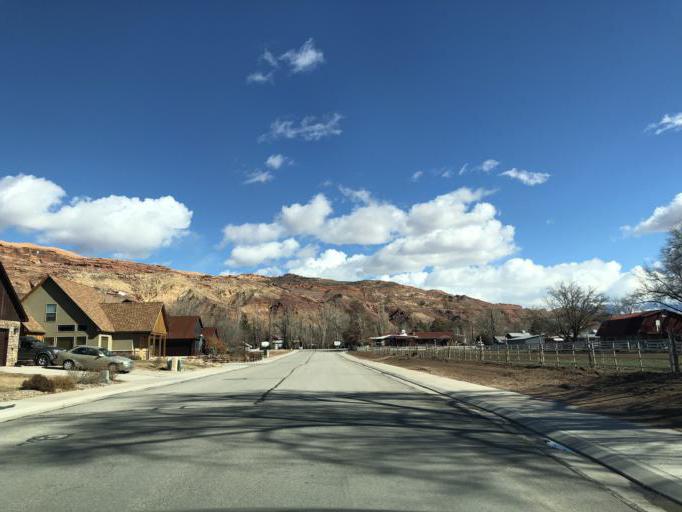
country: US
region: Utah
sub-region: Grand County
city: Moab
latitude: 38.5848
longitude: -109.5636
